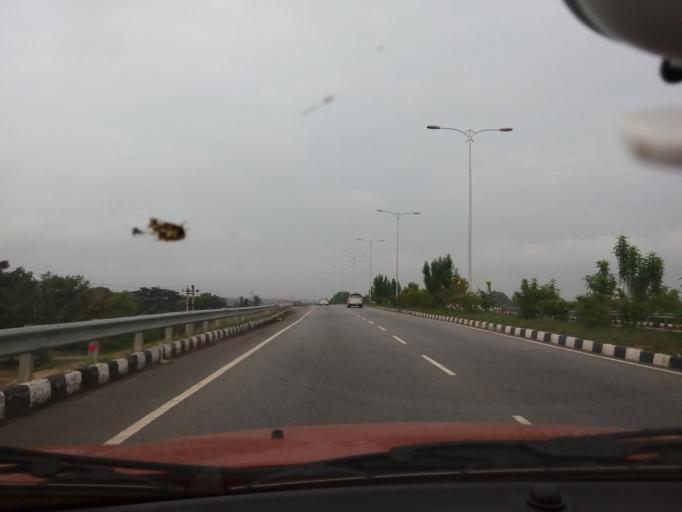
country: IN
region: Karnataka
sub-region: Tumkur
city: Kunigal
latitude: 13.0178
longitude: 77.0459
